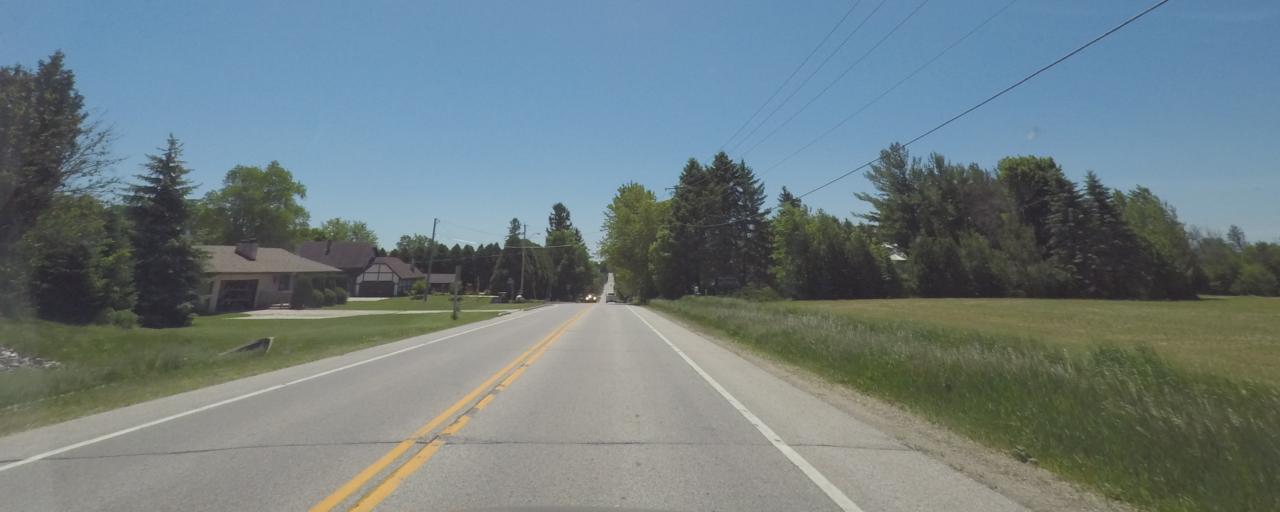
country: US
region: Wisconsin
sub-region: Sheboygan County
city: Random Lake
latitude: 43.5989
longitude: -88.0504
